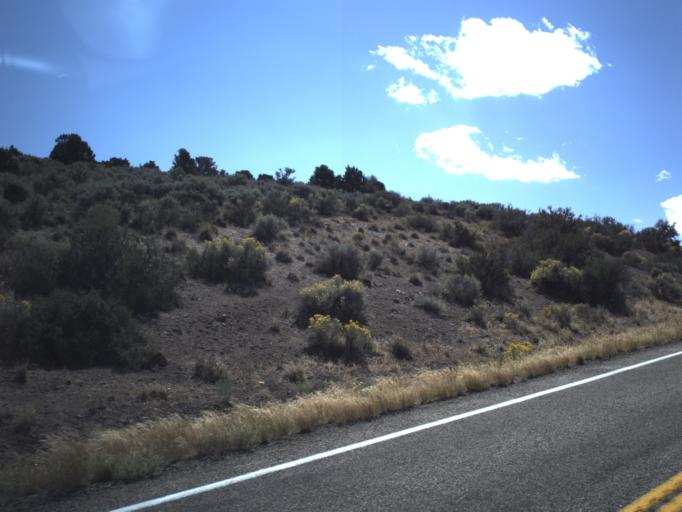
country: US
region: Utah
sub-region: Iron County
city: Parowan
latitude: 38.1069
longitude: -112.9470
